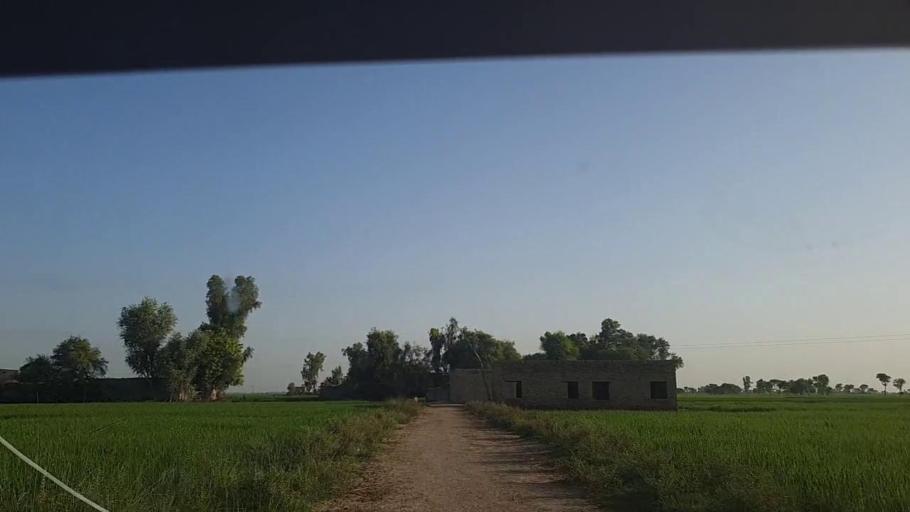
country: PK
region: Sindh
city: Thul
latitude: 28.2113
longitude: 68.8860
